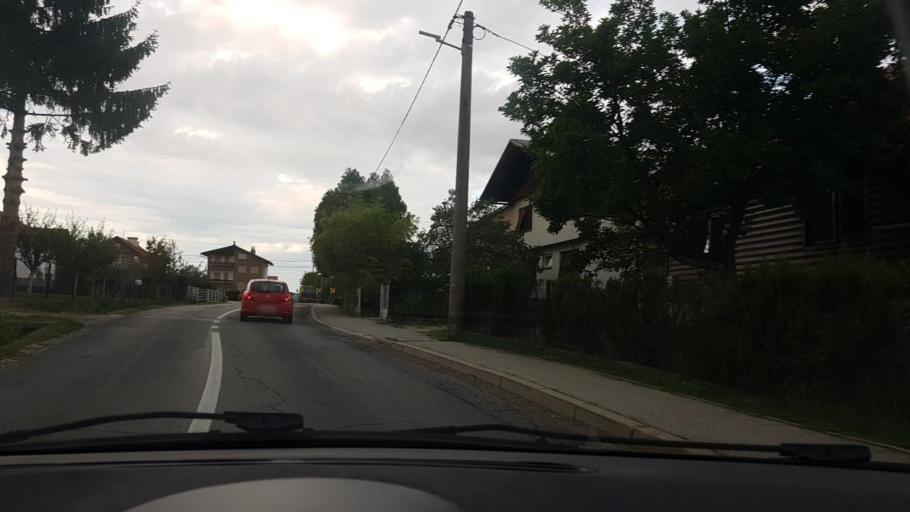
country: HR
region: Krapinsko-Zagorska
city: Oroslavje
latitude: 45.9782
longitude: 15.9260
